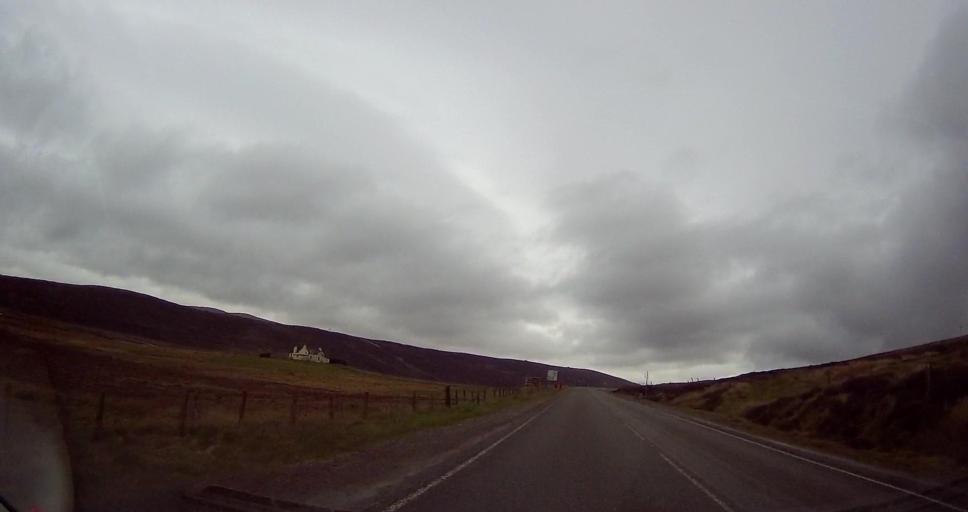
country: GB
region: Scotland
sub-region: Shetland Islands
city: Lerwick
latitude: 60.2762
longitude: -1.2434
